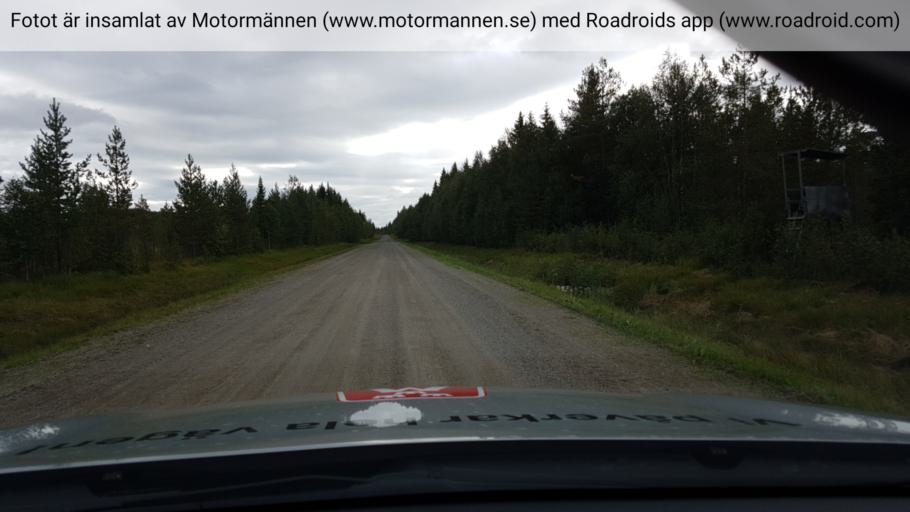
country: SE
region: Jaemtland
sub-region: Ragunda Kommun
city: Hammarstrand
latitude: 62.8832
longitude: 16.0626
